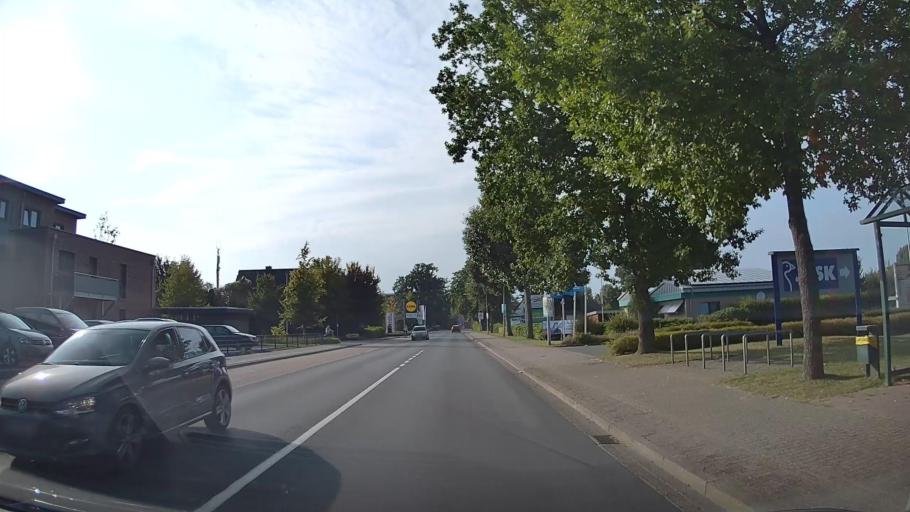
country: DE
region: Lower Saxony
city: Barssel
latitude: 53.1629
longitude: 7.7529
